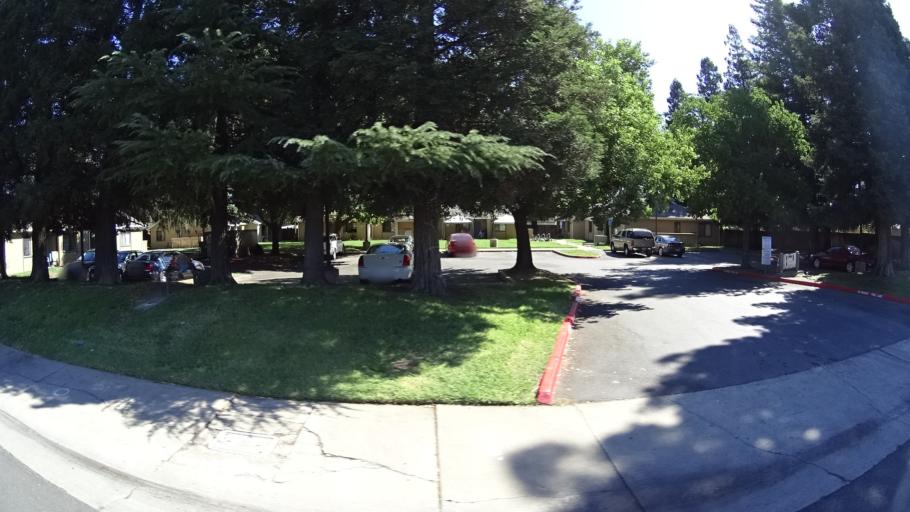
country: US
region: California
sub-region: Sacramento County
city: Elk Grove
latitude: 38.4172
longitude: -121.3715
